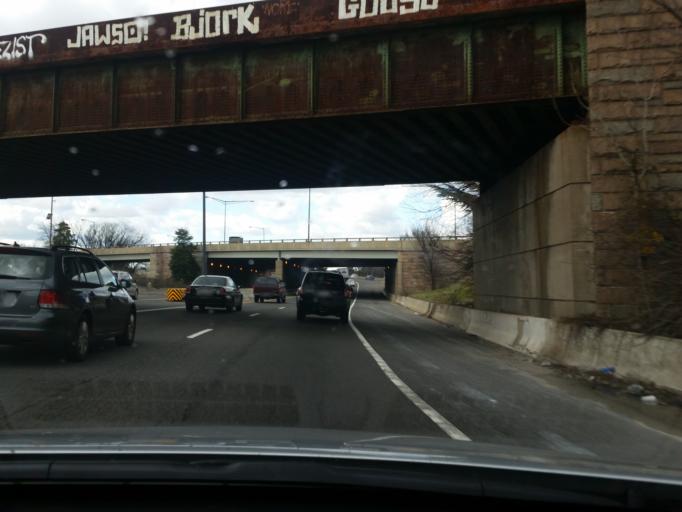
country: US
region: Washington, D.C.
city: Washington, D.C.
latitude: 38.8791
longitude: -77.0346
